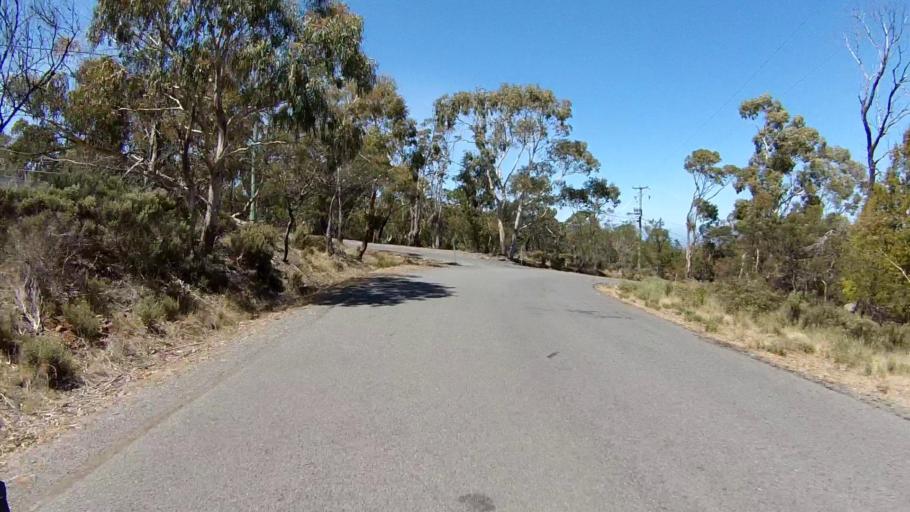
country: AU
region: Tasmania
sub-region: Clarence
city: Cambridge
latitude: -42.8476
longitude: 147.4316
